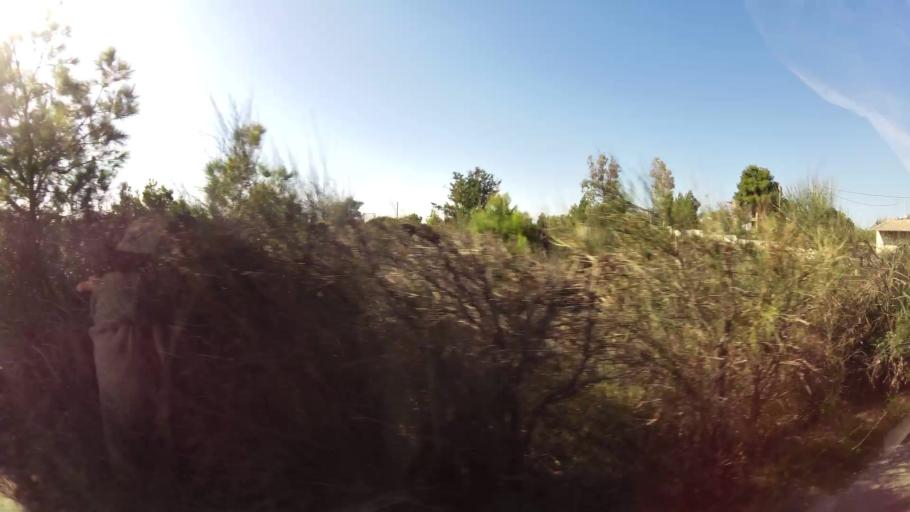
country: GR
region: Attica
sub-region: Nomarchia Anatolikis Attikis
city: Anthousa
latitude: 38.0250
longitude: 23.8679
